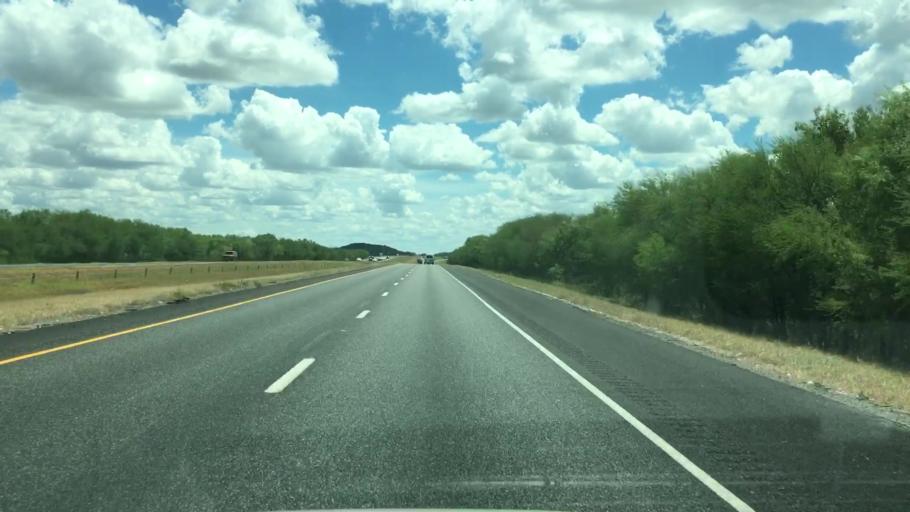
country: US
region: Texas
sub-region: Atascosa County
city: Pleasanton
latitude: 28.7428
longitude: -98.2926
